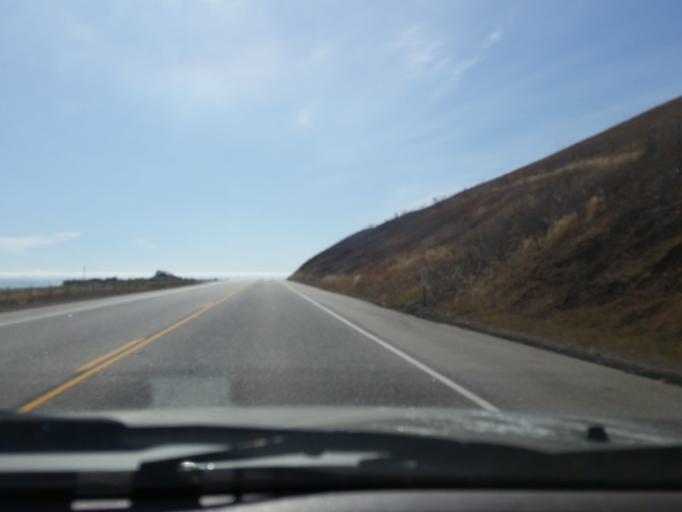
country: US
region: California
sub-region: San Luis Obispo County
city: Cayucos
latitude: 35.4507
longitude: -120.9392
